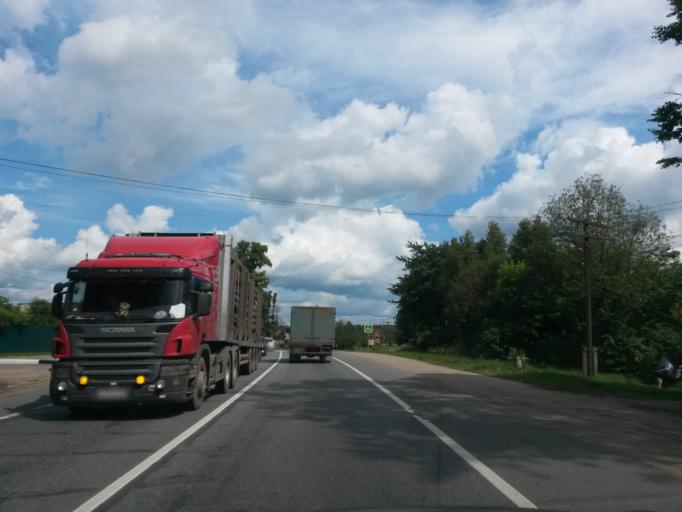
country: RU
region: Jaroslavl
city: Pereslavl'-Zalesskiy
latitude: 56.6533
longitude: 38.6994
